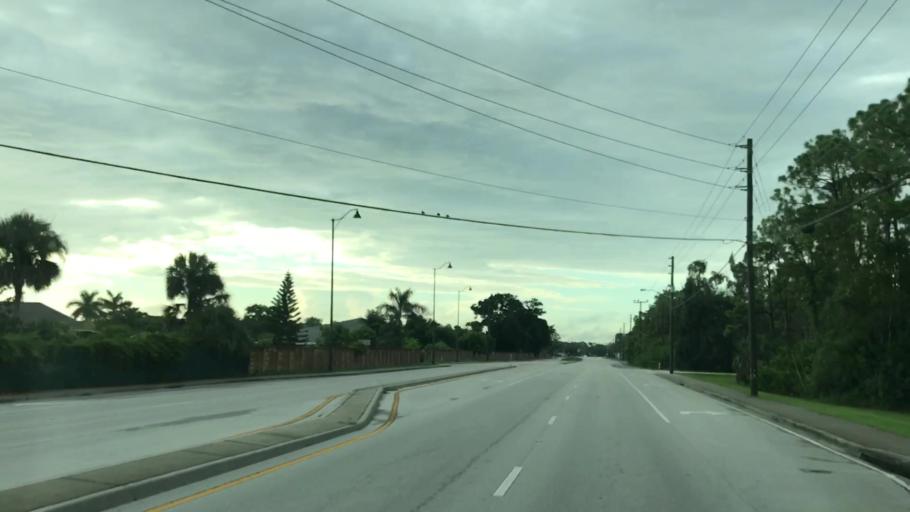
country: US
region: Florida
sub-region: Lee County
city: Bonita Springs
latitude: 26.3594
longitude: -81.7875
